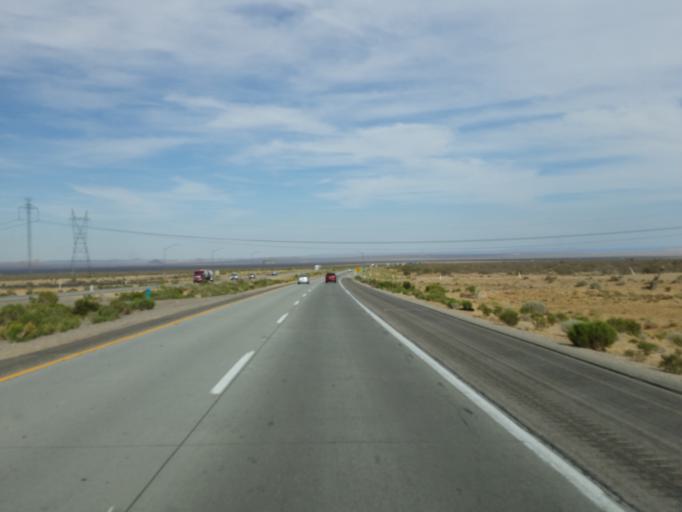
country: US
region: California
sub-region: Kern County
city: Mojave
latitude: 35.1130
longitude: -118.1773
